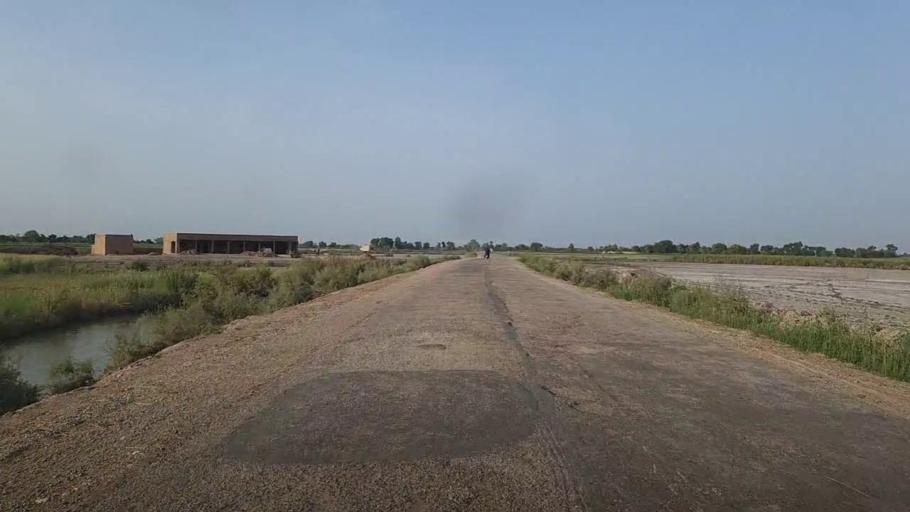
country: PK
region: Sindh
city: Ubauro
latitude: 28.0942
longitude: 69.8065
